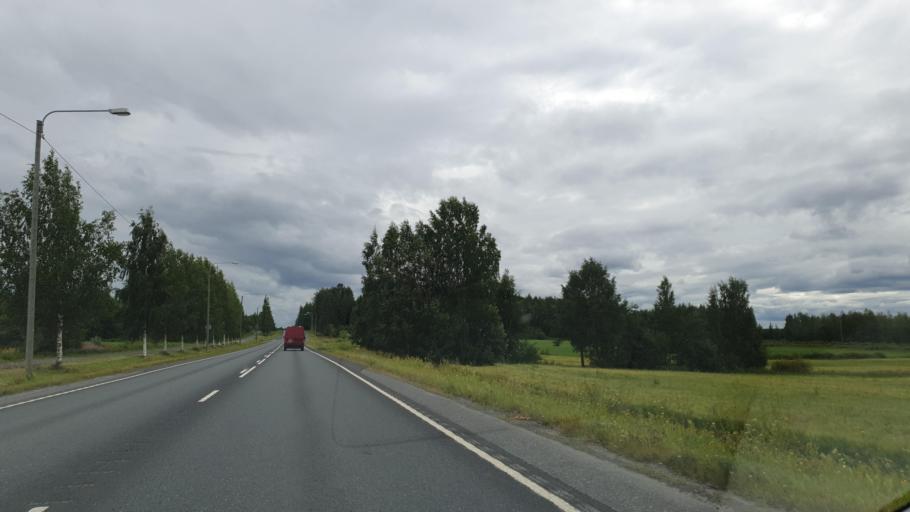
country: FI
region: Northern Savo
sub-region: Ylae-Savo
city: Lapinlahti
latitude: 63.4361
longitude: 27.3261
